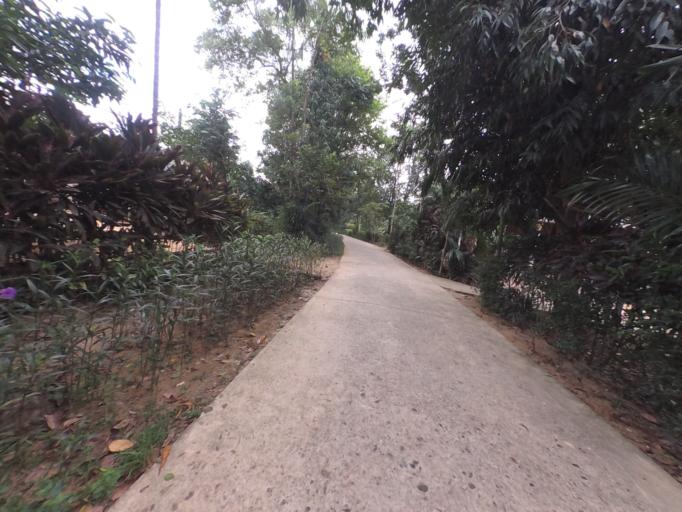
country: VN
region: Thua Thien-Hue
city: A Luoi
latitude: 16.2981
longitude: 107.3488
